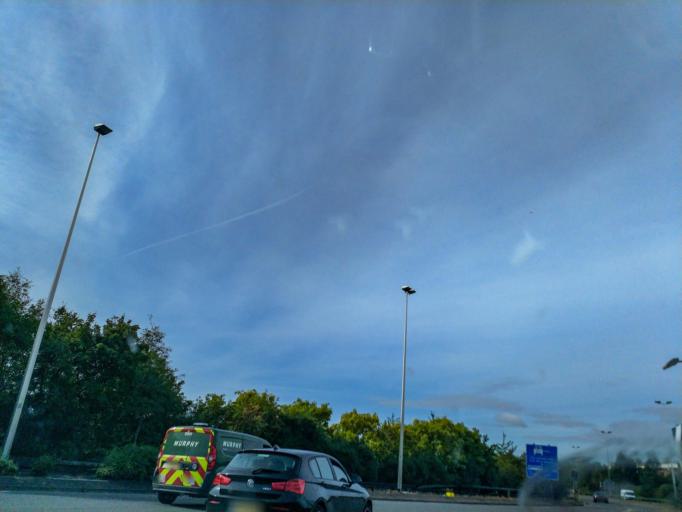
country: GB
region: England
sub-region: City and Borough of Birmingham
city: Birmingham
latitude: 52.4986
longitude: -1.8596
